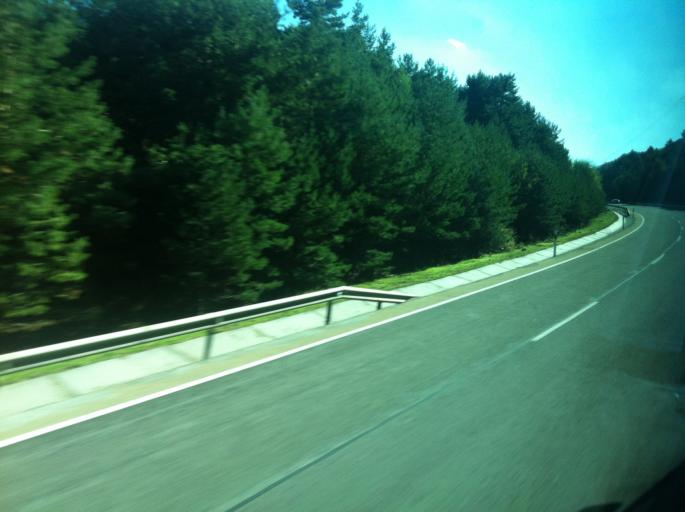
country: ES
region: Madrid
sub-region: Provincia de Madrid
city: Somosierra
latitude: 41.1634
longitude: -3.5851
